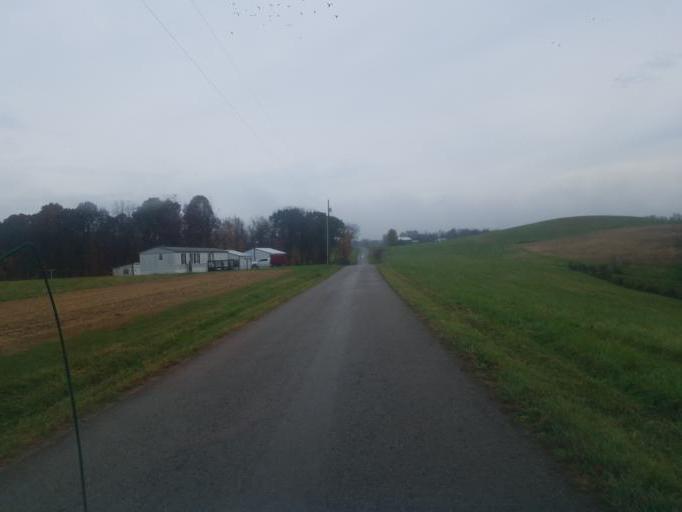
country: US
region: Ohio
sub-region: Morgan County
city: McConnelsville
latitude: 39.5081
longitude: -81.8002
